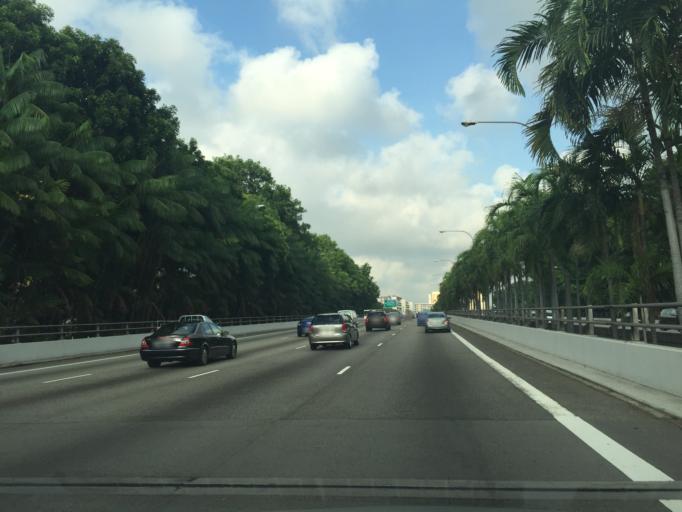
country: SG
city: Singapore
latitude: 1.3217
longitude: 103.8836
